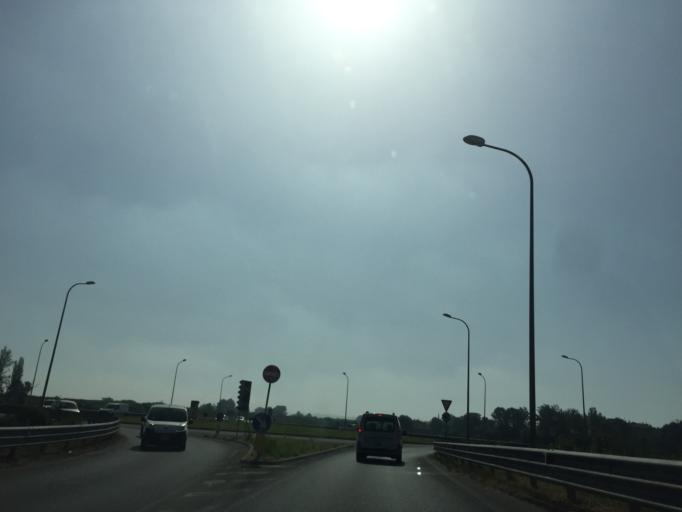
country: IT
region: Tuscany
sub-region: Province of Pisa
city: Montecalvoli
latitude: 43.6723
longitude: 10.6493
